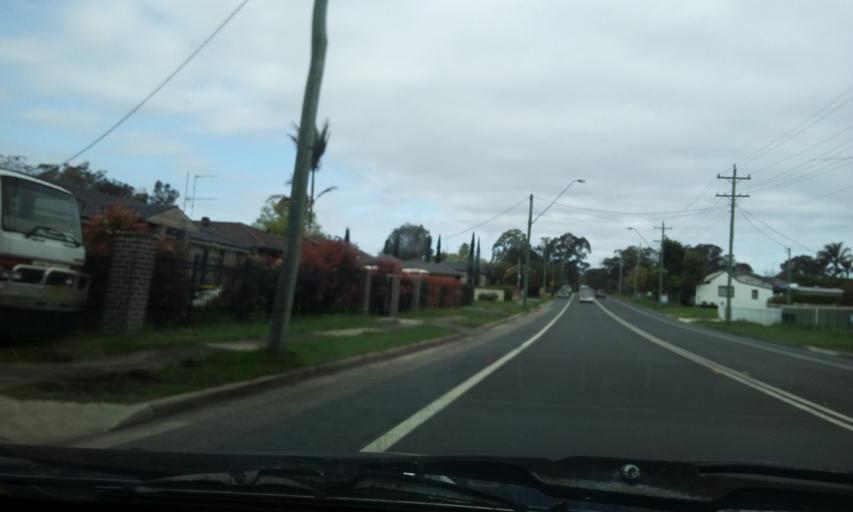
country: AU
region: New South Wales
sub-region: Wollondilly
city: Douglas Park
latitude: -34.2037
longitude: 150.7887
